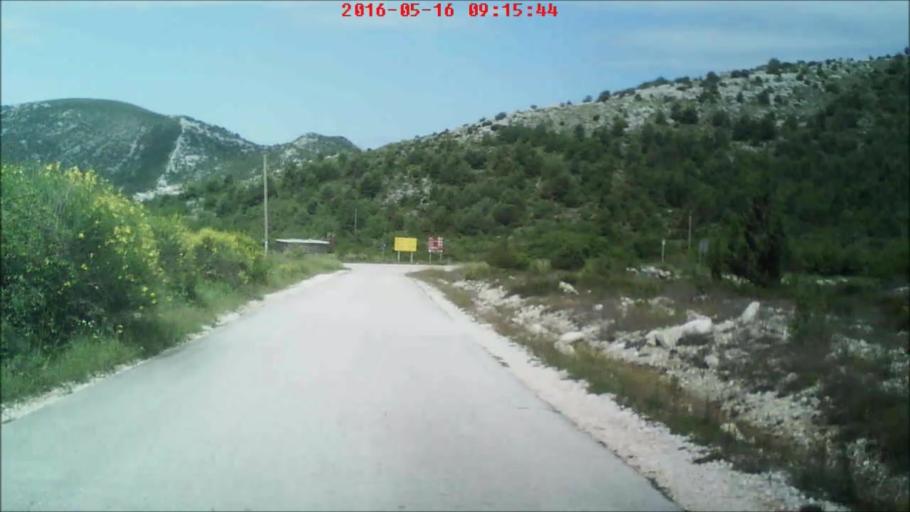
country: HR
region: Dubrovacko-Neretvanska
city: Podgora
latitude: 42.8480
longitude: 17.8383
